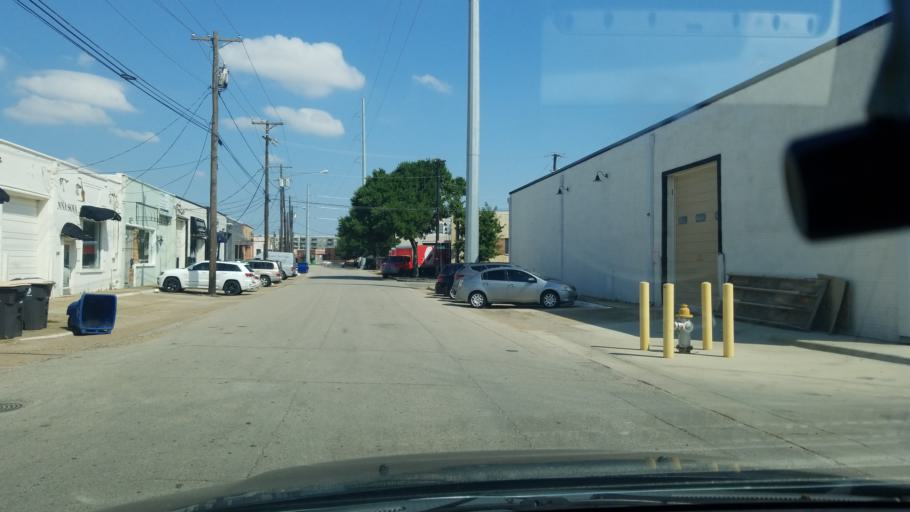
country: US
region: Texas
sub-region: Dallas County
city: Dallas
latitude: 32.7878
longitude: -96.8229
